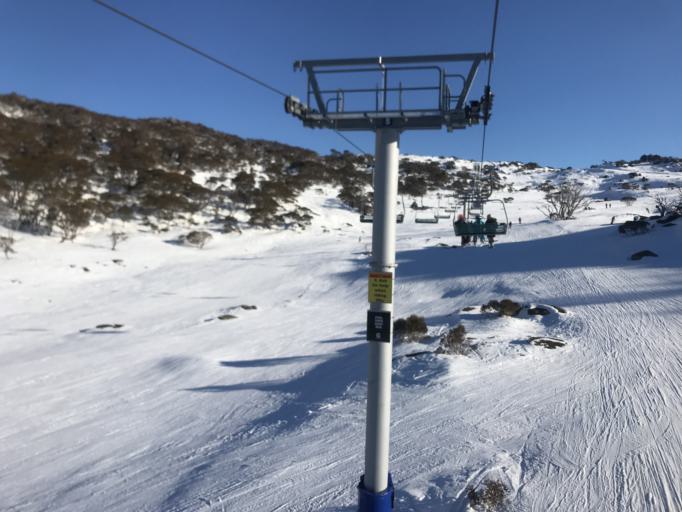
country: AU
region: New South Wales
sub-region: Snowy River
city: Jindabyne
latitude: -36.3889
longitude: 148.3975
